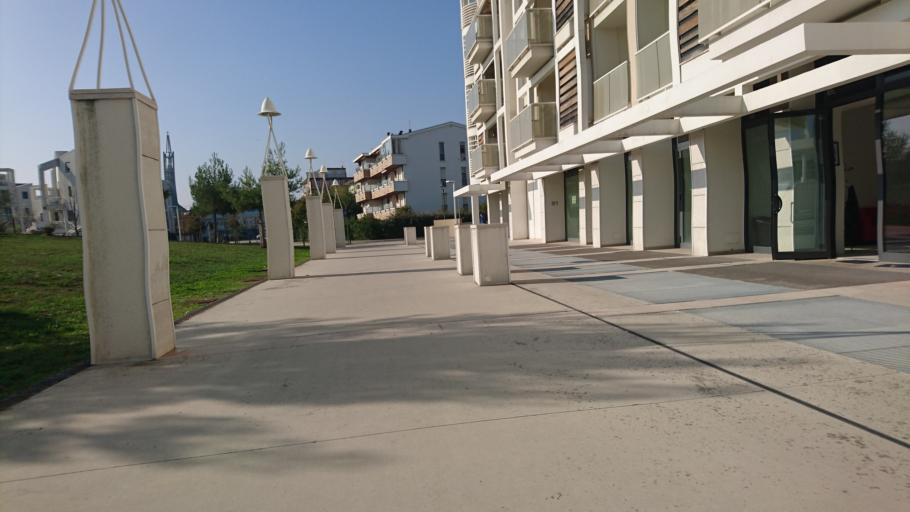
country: IT
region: Emilia-Romagna
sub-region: Provincia di Rimini
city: Rimini
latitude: 44.0737
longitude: 12.5708
